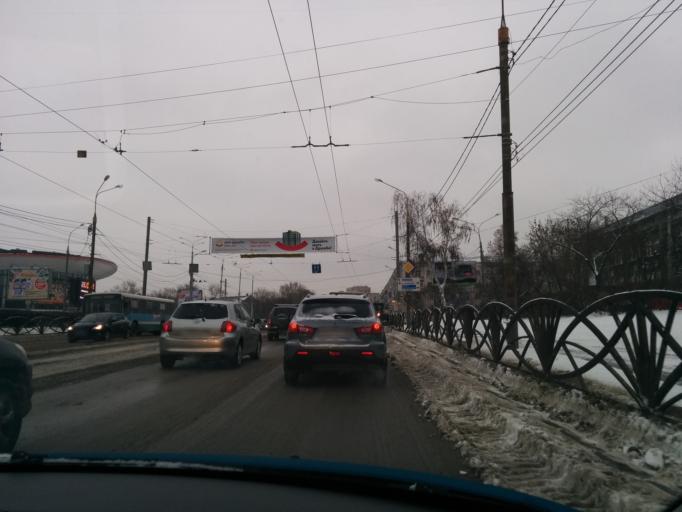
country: RU
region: Perm
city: Perm
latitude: 58.0191
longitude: 56.2747
